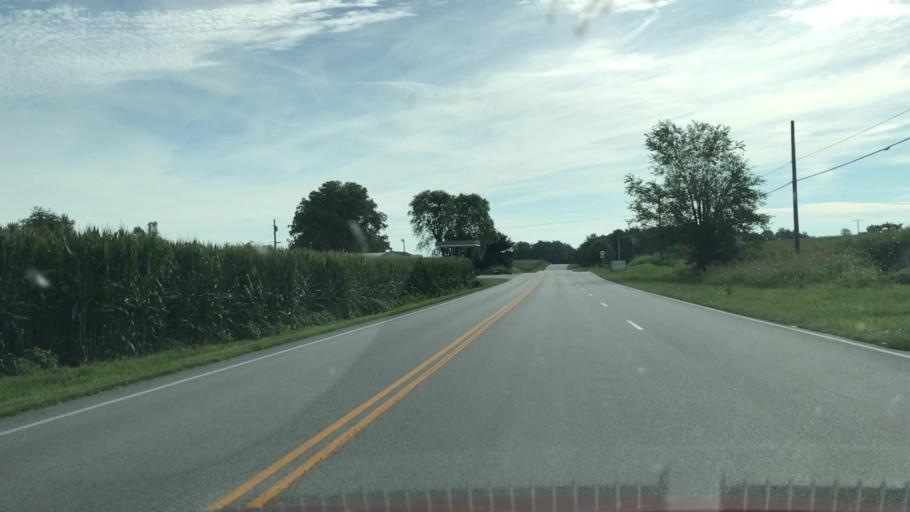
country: US
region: Kentucky
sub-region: Edmonson County
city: Brownsville
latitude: 37.0701
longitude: -86.2686
